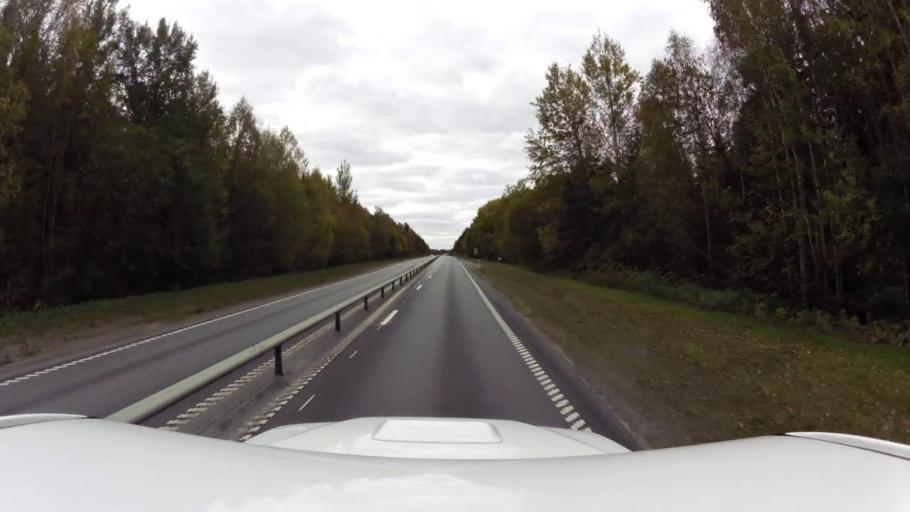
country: SE
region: OEstergoetland
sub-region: Linkopings Kommun
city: Malmslatt
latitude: 58.3797
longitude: 15.5424
